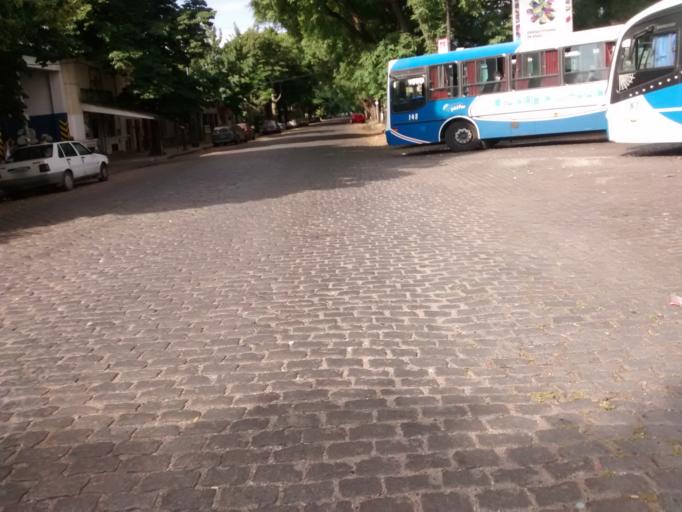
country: AR
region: Buenos Aires
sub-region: Partido de La Plata
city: La Plata
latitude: -34.9395
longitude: -57.9392
